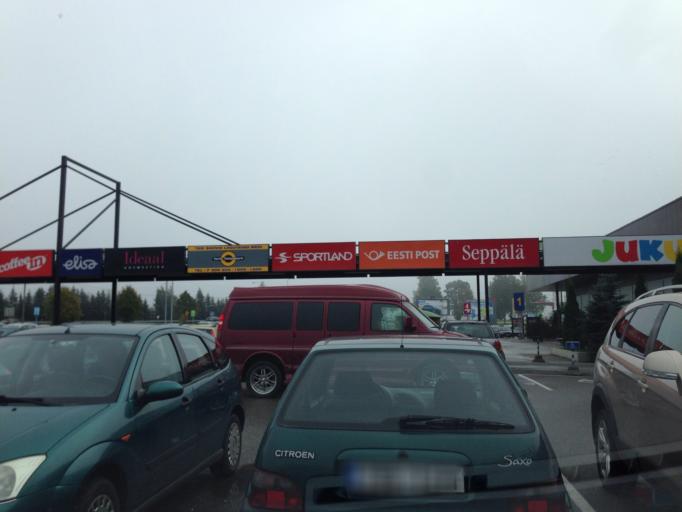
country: EE
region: Tartu
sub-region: Tartu linn
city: Tartu
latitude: 58.3586
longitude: 26.6783
